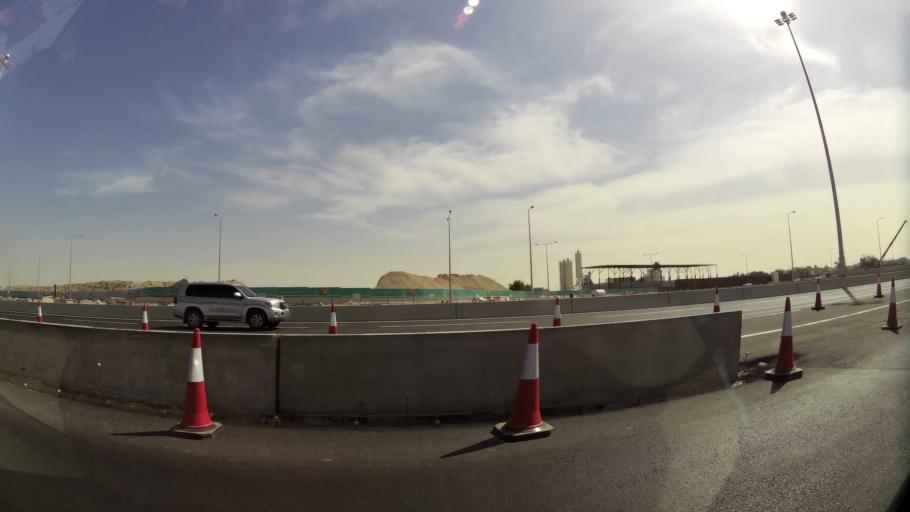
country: QA
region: Baladiyat ar Rayyan
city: Ar Rayyan
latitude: 25.3013
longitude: 51.4255
